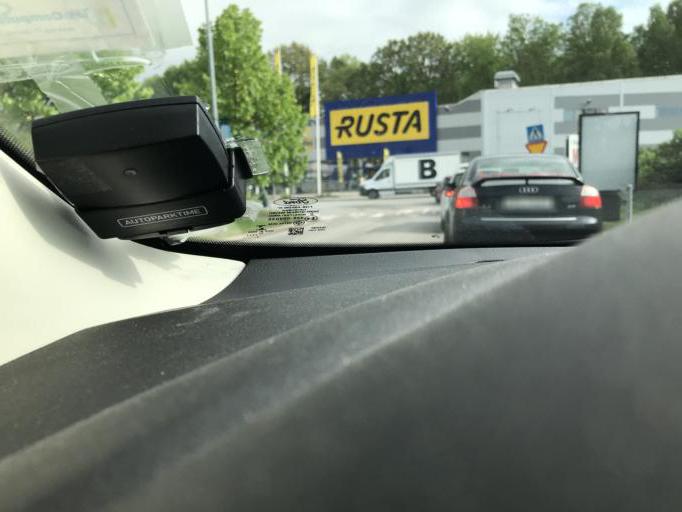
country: SE
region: Stockholm
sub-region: Botkyrka Kommun
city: Eriksberg
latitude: 59.2370
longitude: 17.8340
